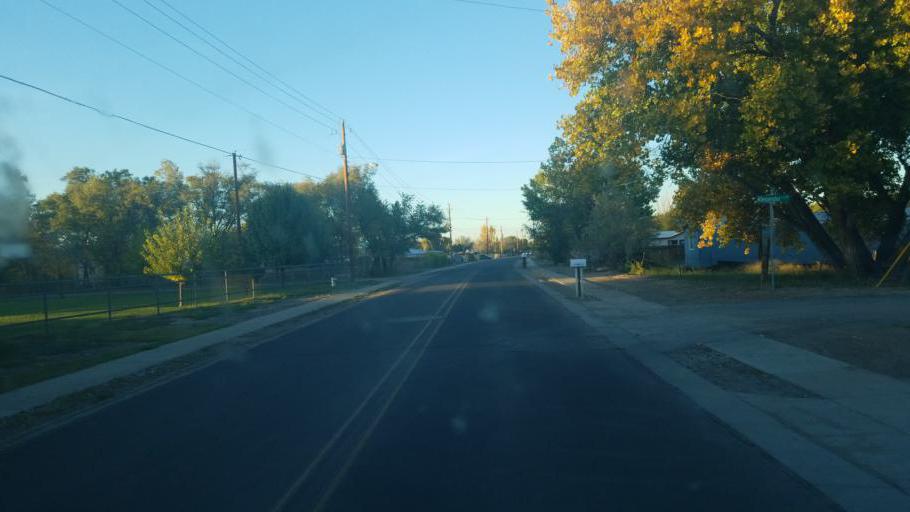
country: US
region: New Mexico
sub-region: Valencia County
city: Los Lunas
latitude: 34.8253
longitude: -106.7241
